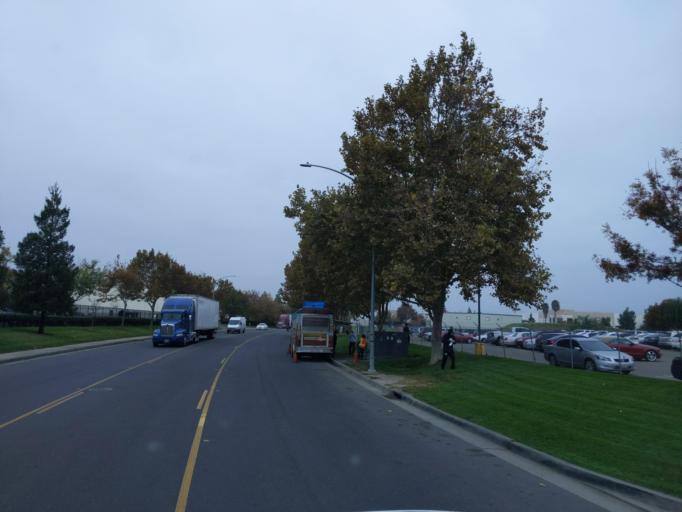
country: US
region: California
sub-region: San Joaquin County
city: Kennedy
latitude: 37.9100
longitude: -121.2460
